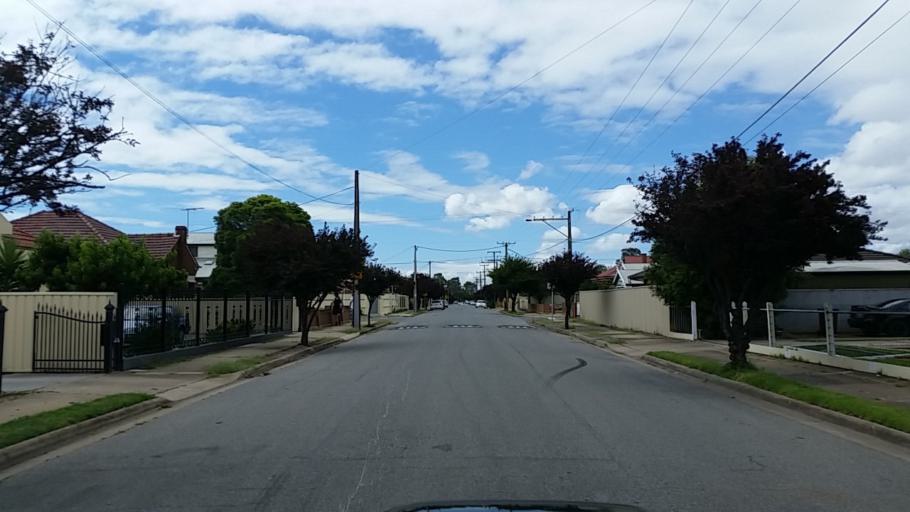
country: AU
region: South Australia
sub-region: Charles Sturt
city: Allenby Gardens
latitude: -34.8953
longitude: 138.5492
